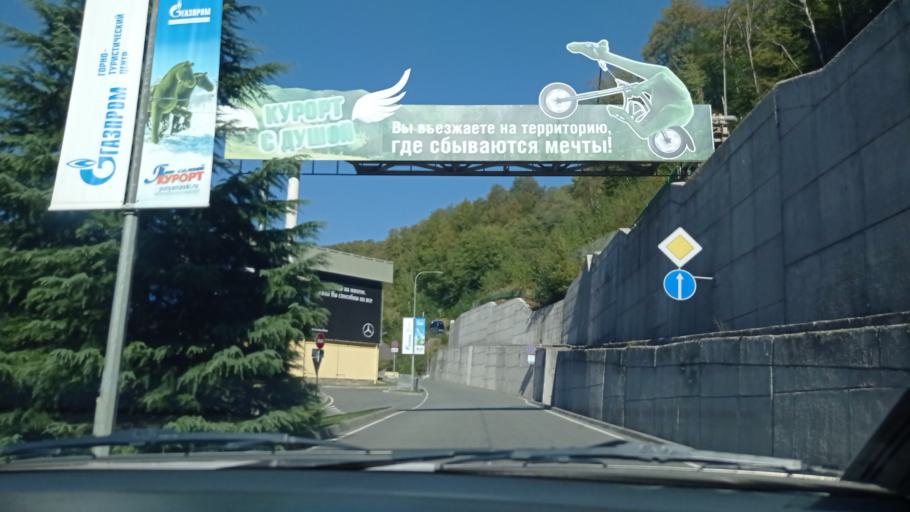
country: RU
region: Krasnodarskiy
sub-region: Sochi City
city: Krasnaya Polyana
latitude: 43.6831
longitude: 40.2805
